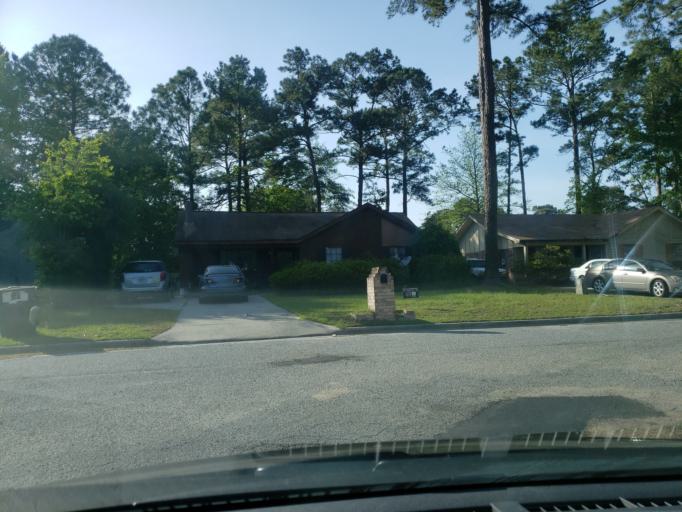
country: US
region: Georgia
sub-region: Chatham County
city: Isle of Hope
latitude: 31.9934
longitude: -81.0713
